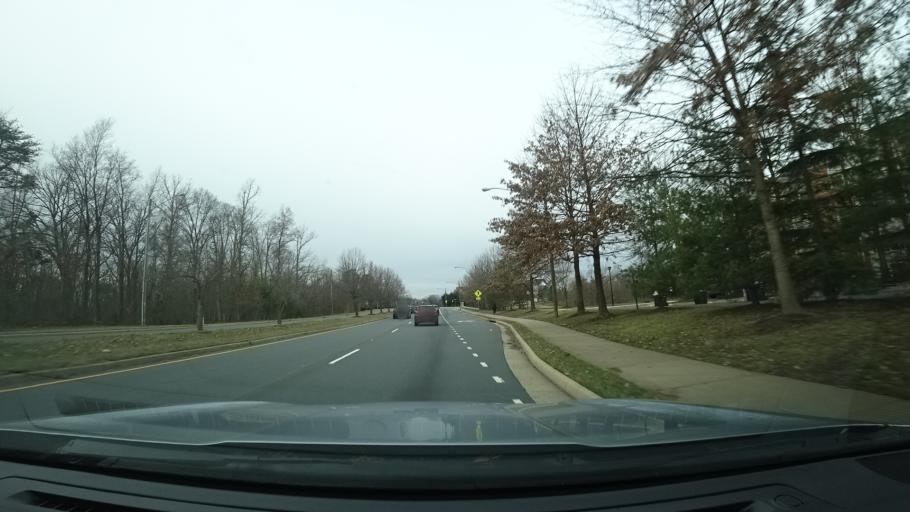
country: US
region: Virginia
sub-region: Fairfax County
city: Floris
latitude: 38.9433
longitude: -77.4035
